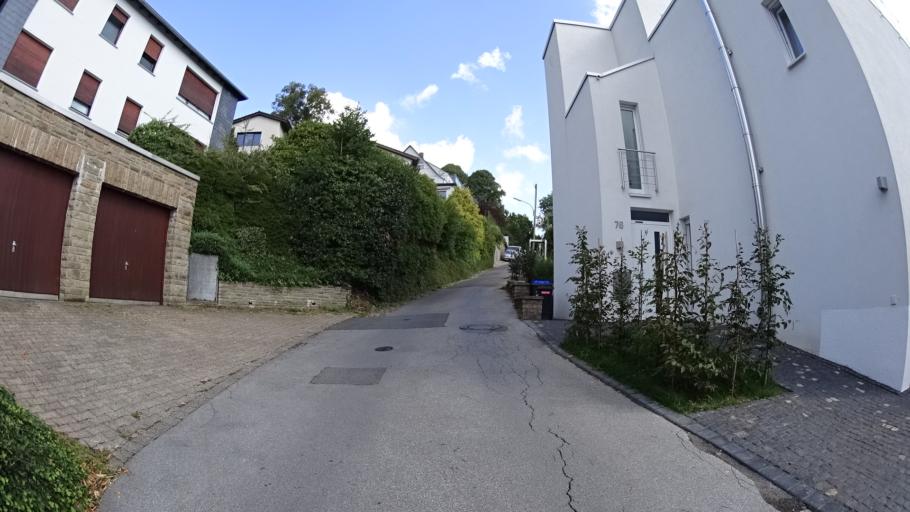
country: DE
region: North Rhine-Westphalia
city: Witten
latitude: 51.4324
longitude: 7.3475
